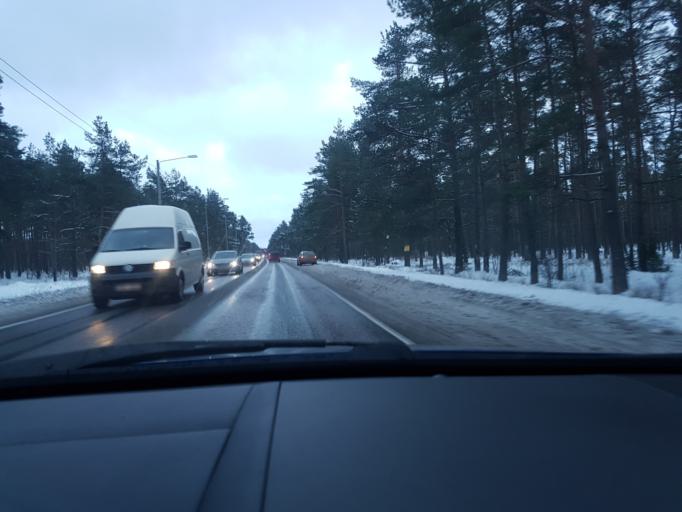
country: EE
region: Harju
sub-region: Tallinna linn
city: Tallinn
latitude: 59.3802
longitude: 24.7422
